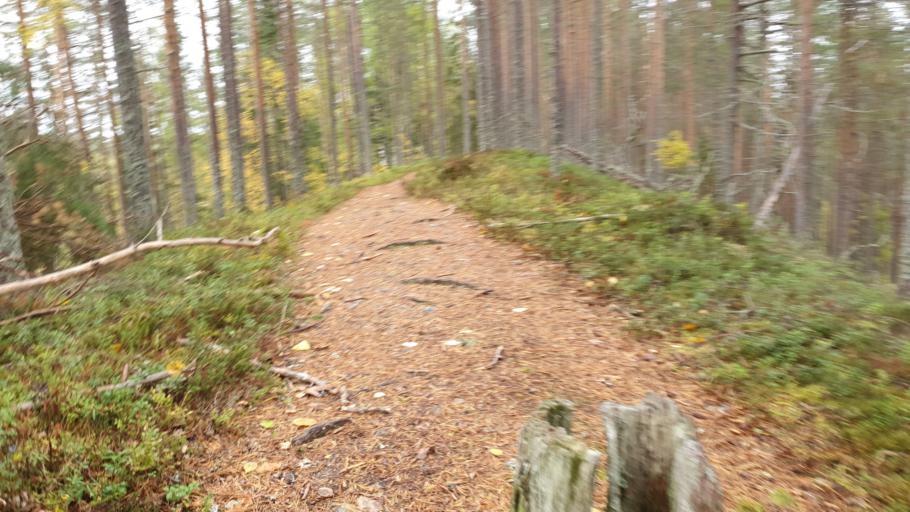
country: FI
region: Kainuu
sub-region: Kehys-Kainuu
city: Kuhmo
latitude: 64.2938
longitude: 29.3798
